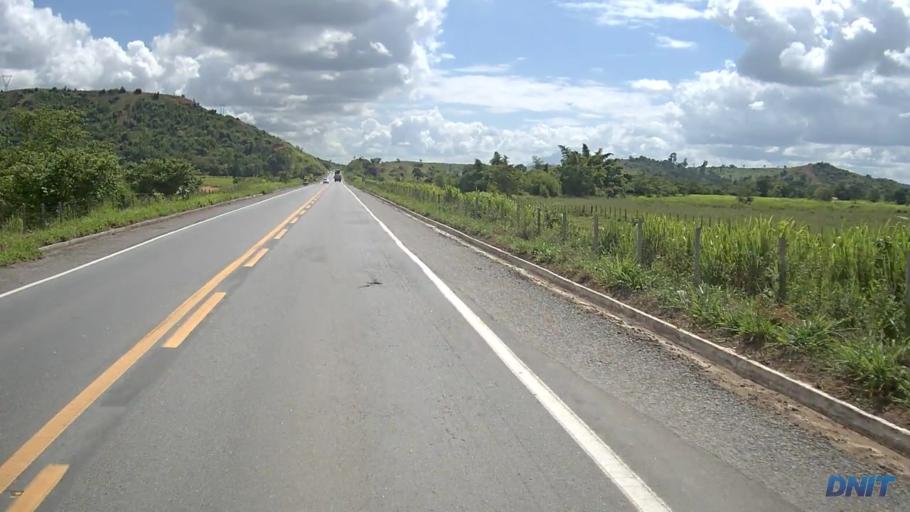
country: BR
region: Minas Gerais
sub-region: Governador Valadares
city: Governador Valadares
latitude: -19.0017
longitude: -42.1265
